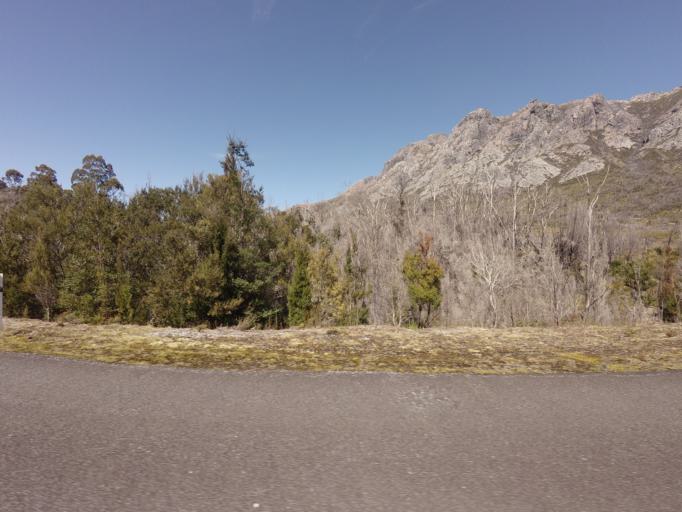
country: AU
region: Tasmania
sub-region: Huon Valley
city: Geeveston
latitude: -42.8586
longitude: 146.2299
